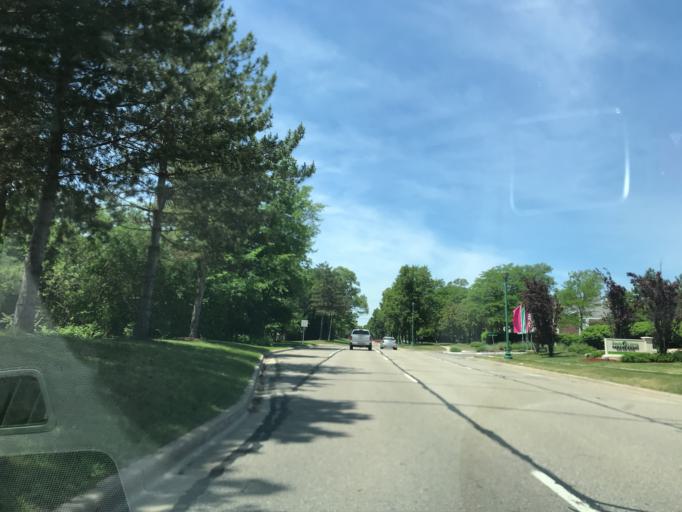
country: US
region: Michigan
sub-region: Oakland County
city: Bingham Farms
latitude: 42.4793
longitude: -83.2721
